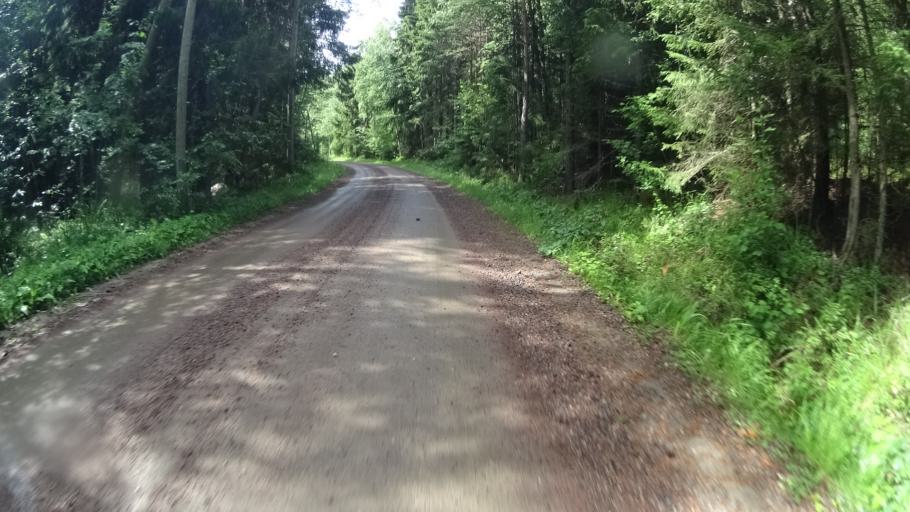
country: FI
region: Uusimaa
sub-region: Helsinki
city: Karkkila
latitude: 60.5867
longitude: 24.3152
